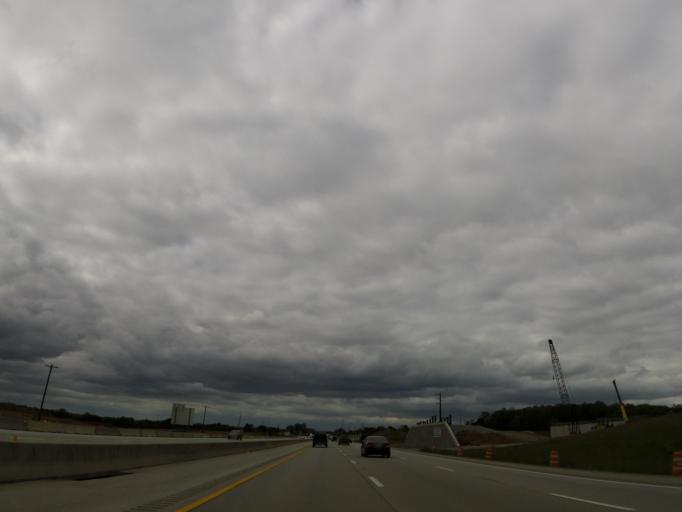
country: US
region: Kentucky
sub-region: Scott County
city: Georgetown
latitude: 38.2411
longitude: -84.5448
